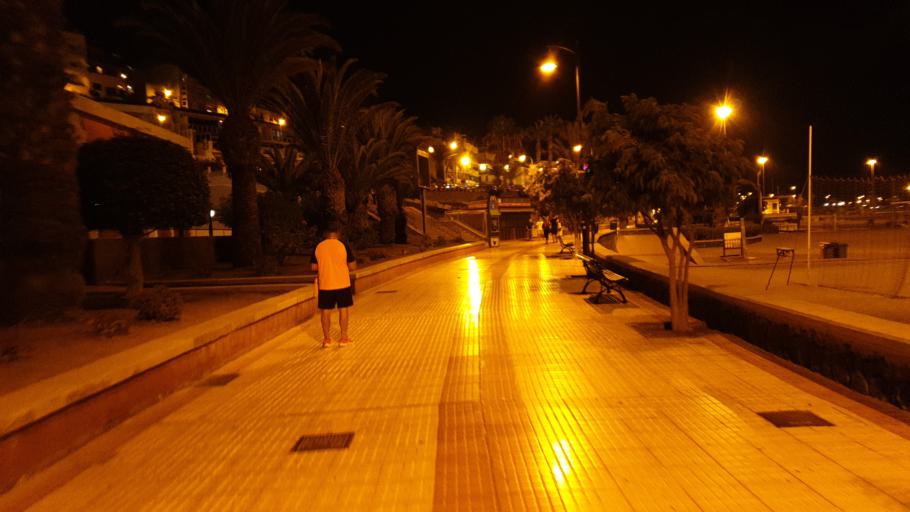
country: ES
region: Canary Islands
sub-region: Provincia de Santa Cruz de Tenerife
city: Playa de las Americas
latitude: 28.0530
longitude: -16.7242
